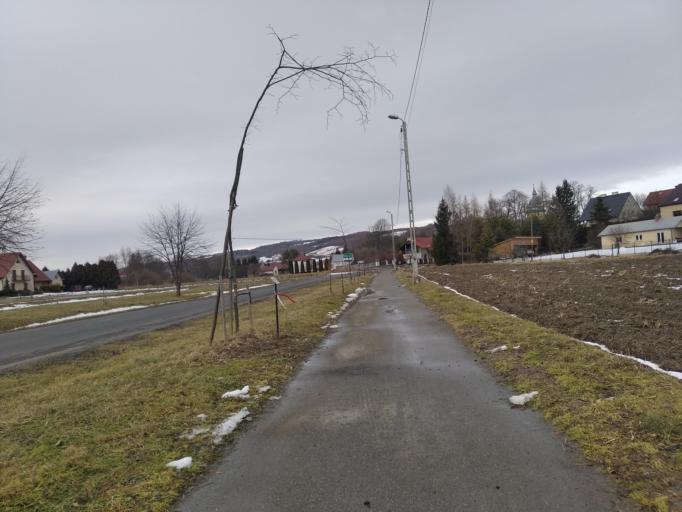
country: PL
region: Subcarpathian Voivodeship
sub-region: Powiat przemyski
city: Dubiecko
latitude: 49.8240
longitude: 22.3888
